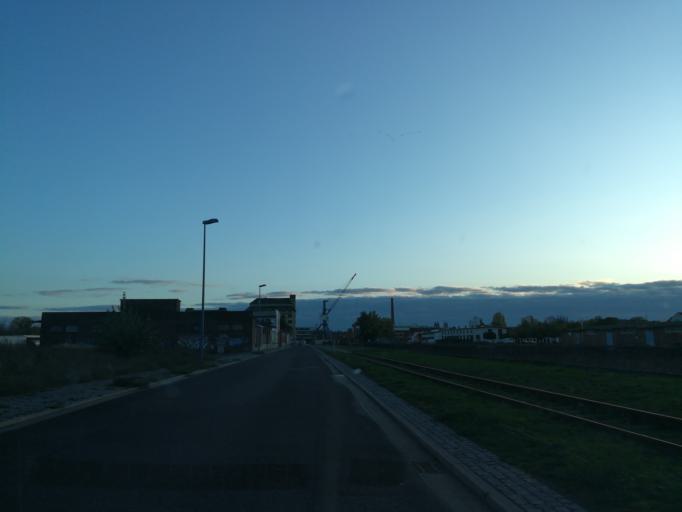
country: DE
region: Saxony-Anhalt
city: Neue Neustadt
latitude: 52.1450
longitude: 11.6592
